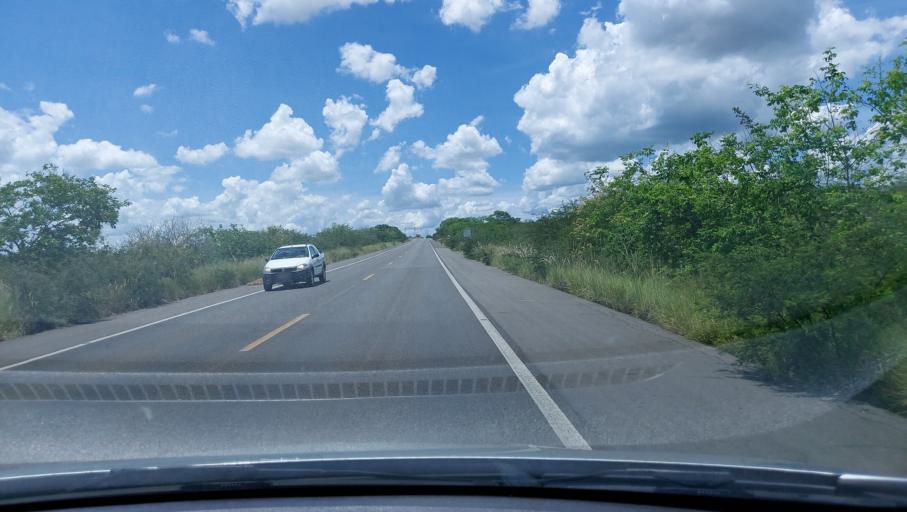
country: BR
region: Bahia
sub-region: Itaberaba
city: Itaberaba
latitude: -12.5212
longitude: -40.2717
